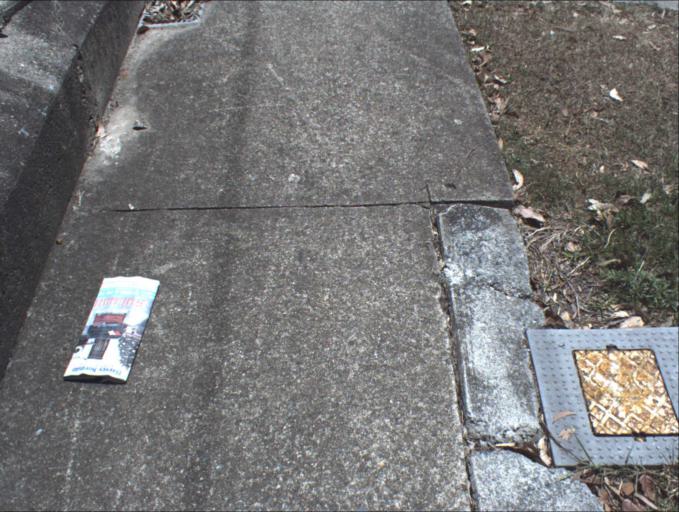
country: AU
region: Queensland
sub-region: Gold Coast
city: Yatala
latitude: -27.7122
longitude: 153.2140
